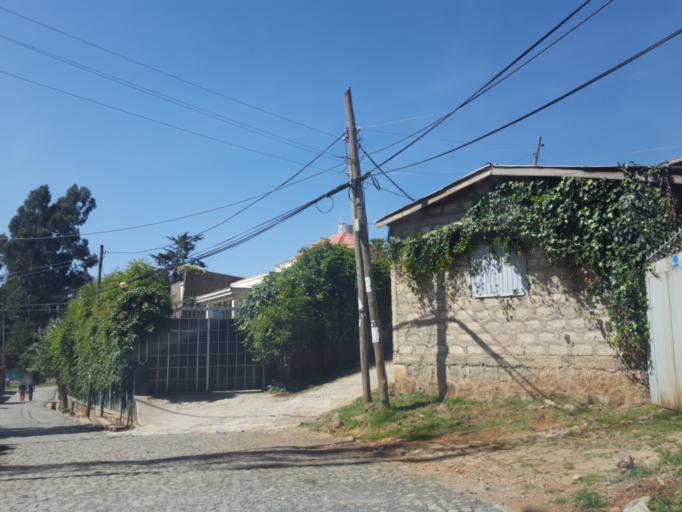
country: ET
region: Adis Abeba
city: Addis Ababa
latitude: 9.0624
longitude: 38.7446
